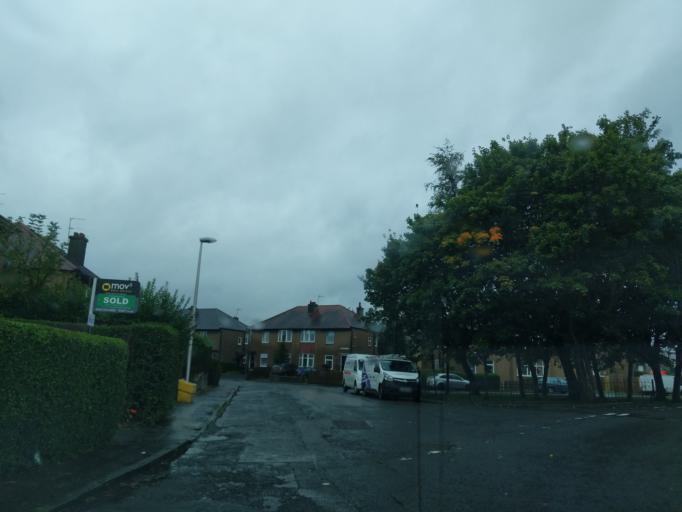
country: GB
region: Scotland
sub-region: Edinburgh
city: Colinton
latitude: 55.9351
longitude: -3.2844
